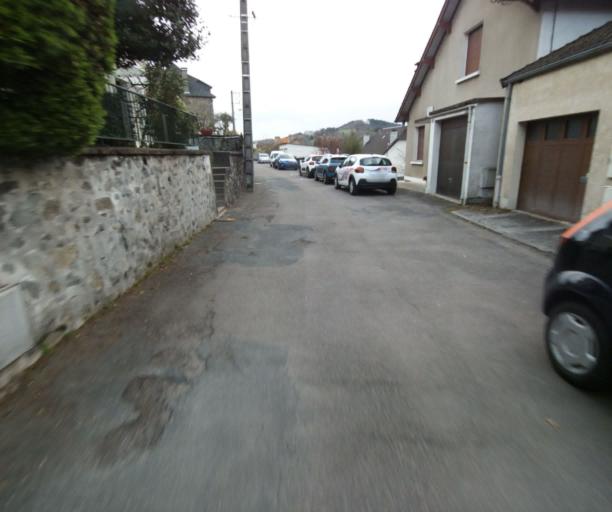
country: FR
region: Limousin
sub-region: Departement de la Correze
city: Tulle
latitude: 45.2591
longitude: 1.7586
